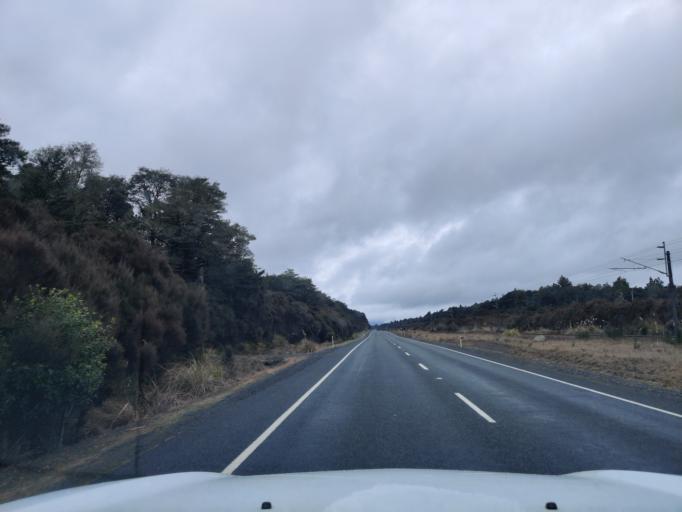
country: NZ
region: Manawatu-Wanganui
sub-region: Ruapehu District
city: Waiouru
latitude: -39.3157
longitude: 175.3874
